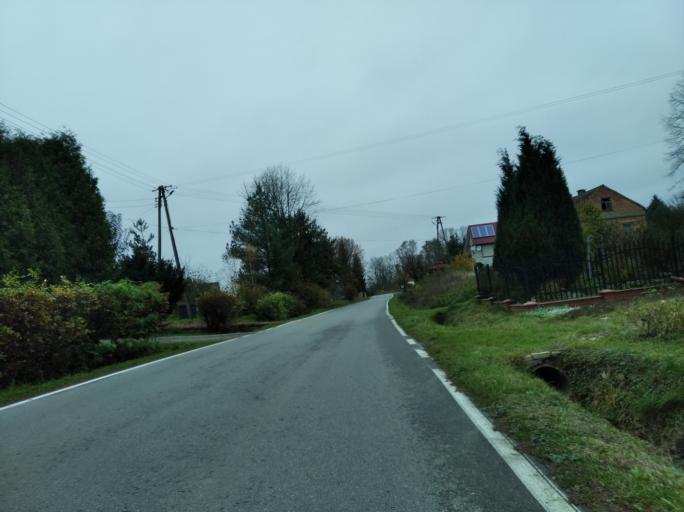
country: PL
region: Subcarpathian Voivodeship
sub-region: Powiat krosnienski
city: Leki
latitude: 49.8069
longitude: 21.6610
